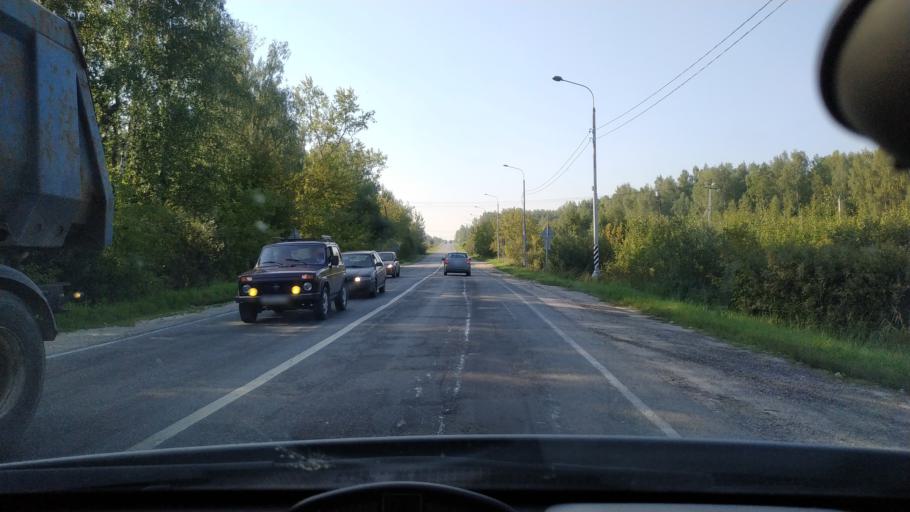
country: RU
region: Moskovskaya
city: Tugolesskiy Bor
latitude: 55.5599
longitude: 39.7023
